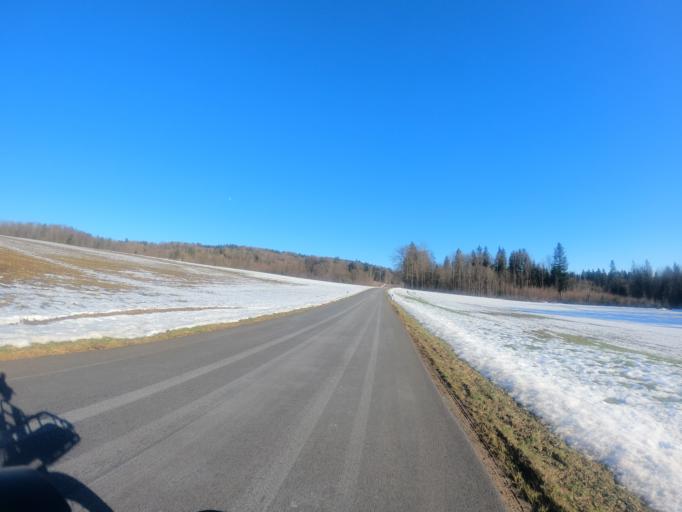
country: CH
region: Aargau
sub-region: Bezirk Bremgarten
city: Jonen
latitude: 47.3029
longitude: 8.4133
